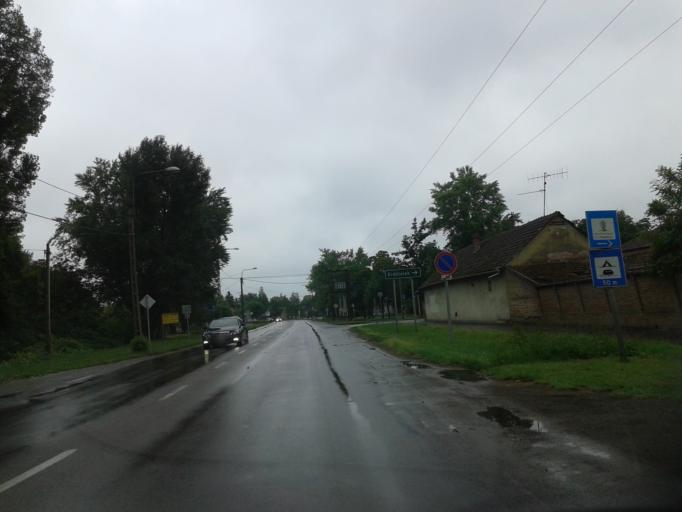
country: HU
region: Bacs-Kiskun
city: Kiskoros
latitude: 46.6234
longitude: 19.2761
